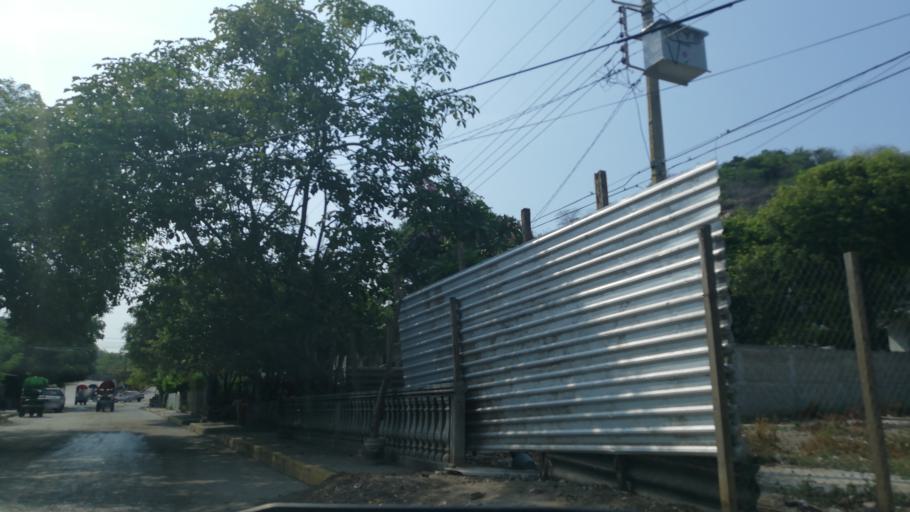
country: MX
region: Oaxaca
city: San Blas Atempa
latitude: 16.3353
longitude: -95.2250
